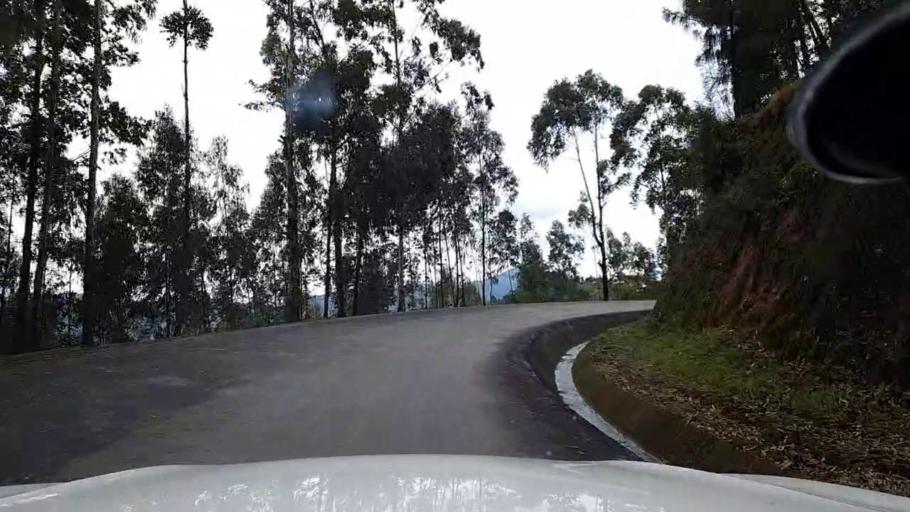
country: RW
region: Western Province
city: Kibuye
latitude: -2.0690
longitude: 29.5404
